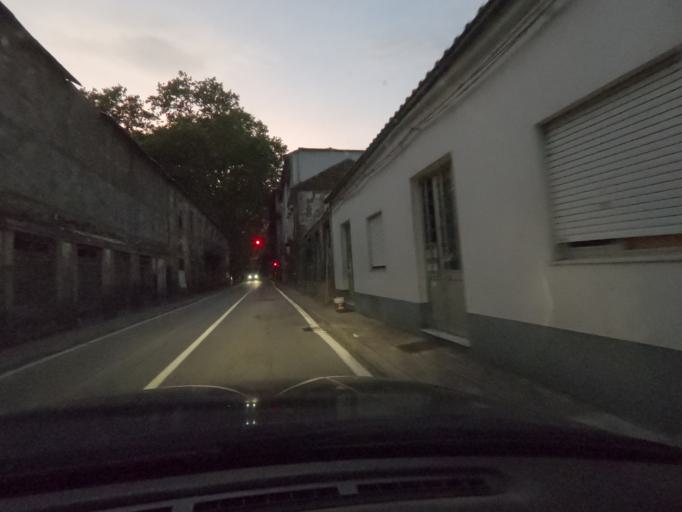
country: PT
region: Vila Real
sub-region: Peso da Regua
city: Godim
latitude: 41.1543
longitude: -7.8340
